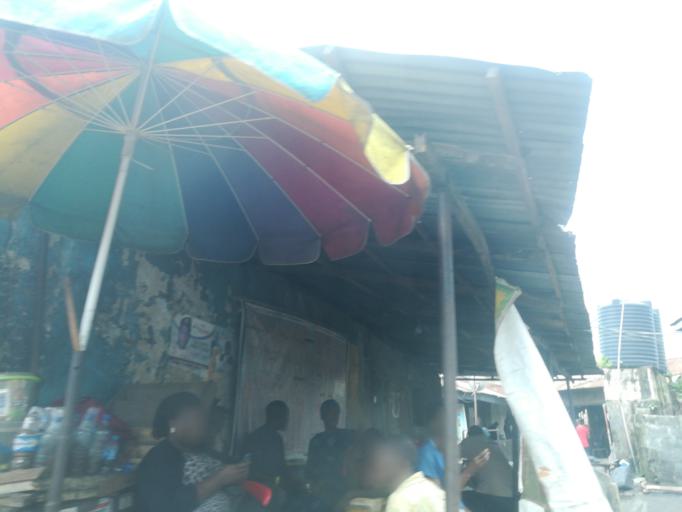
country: NG
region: Lagos
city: Ikeja
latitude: 6.5948
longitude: 3.3435
